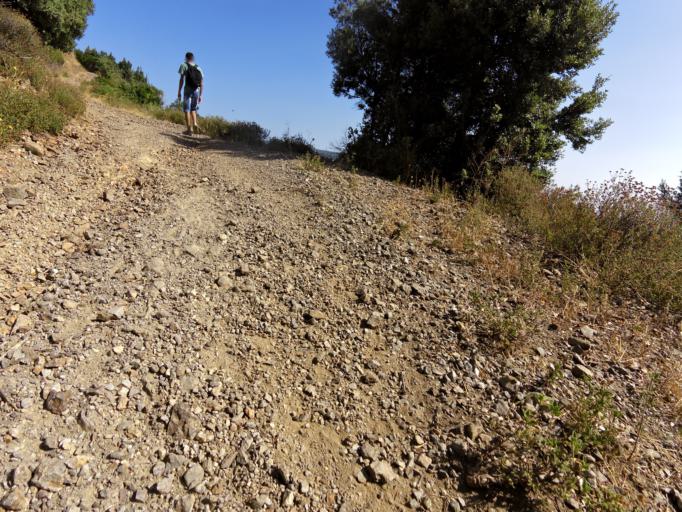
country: IT
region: Calabria
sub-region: Provincia di Reggio Calabria
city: Bivongi
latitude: 38.5001
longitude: 16.4511
